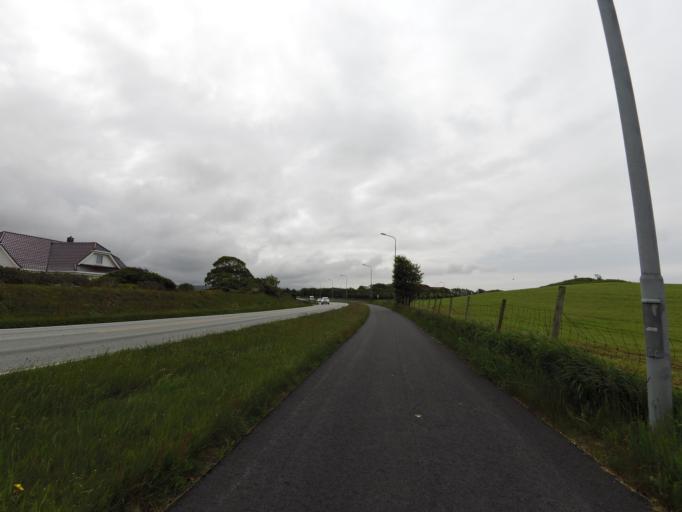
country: NO
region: Rogaland
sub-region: Klepp
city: Kleppe
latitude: 58.8225
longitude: 5.5885
